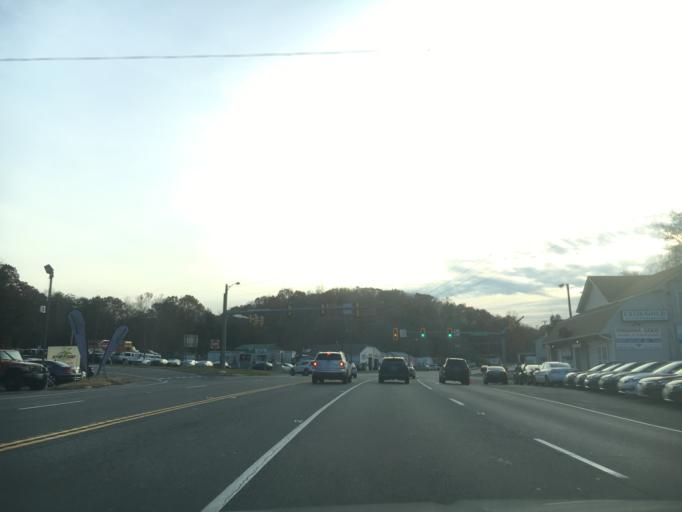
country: US
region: Virginia
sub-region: Stafford County
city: Aquia Harbour
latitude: 38.5081
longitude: -77.3715
